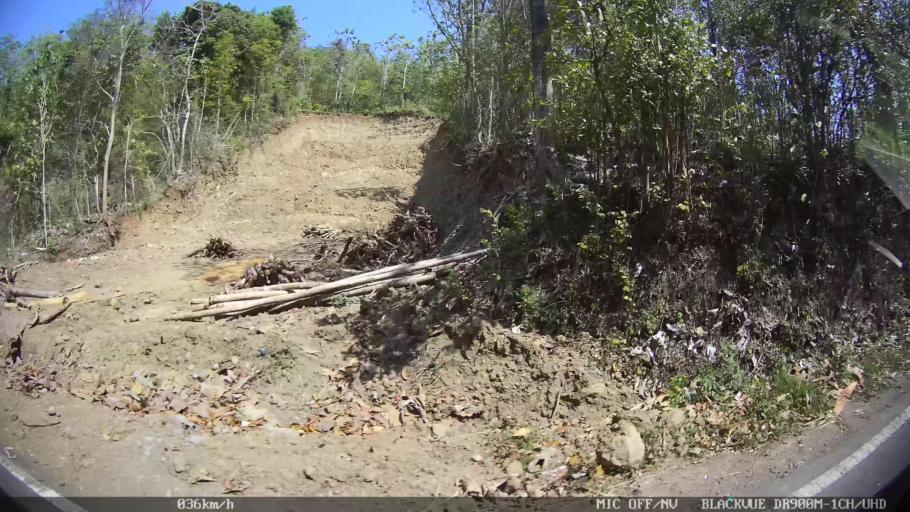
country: ID
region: Daerah Istimewa Yogyakarta
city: Pundong
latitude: -7.9593
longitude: 110.3789
